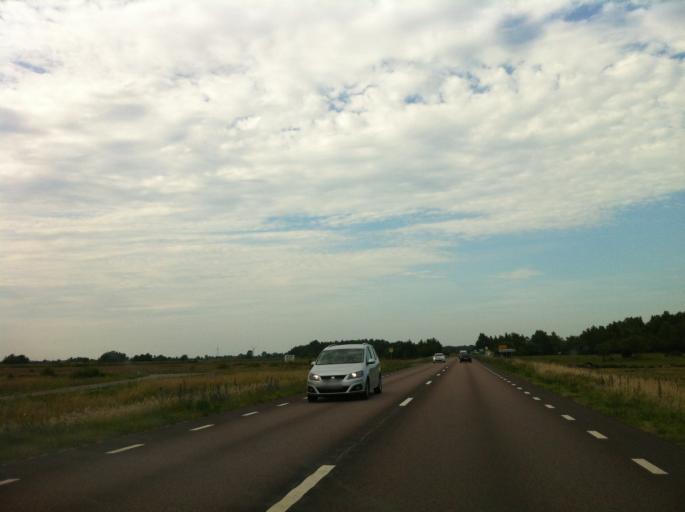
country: SE
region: Kalmar
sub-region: Borgholms Kommun
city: Borgholm
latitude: 57.0474
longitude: 16.8736
